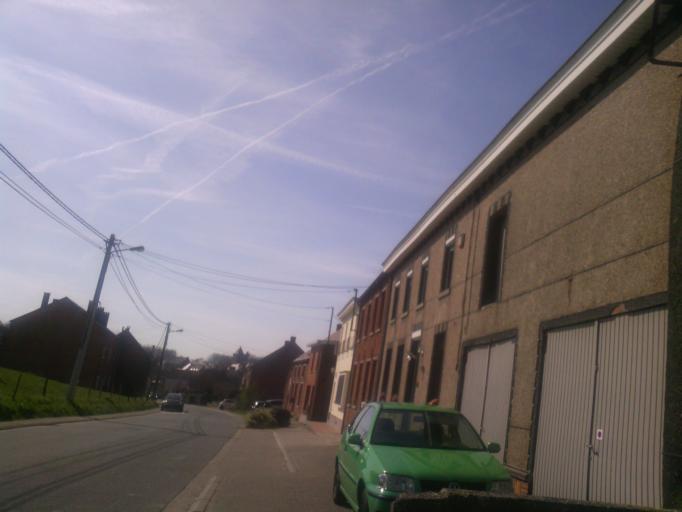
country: BE
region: Wallonia
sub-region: Province du Hainaut
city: Silly
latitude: 50.6518
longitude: 3.9285
